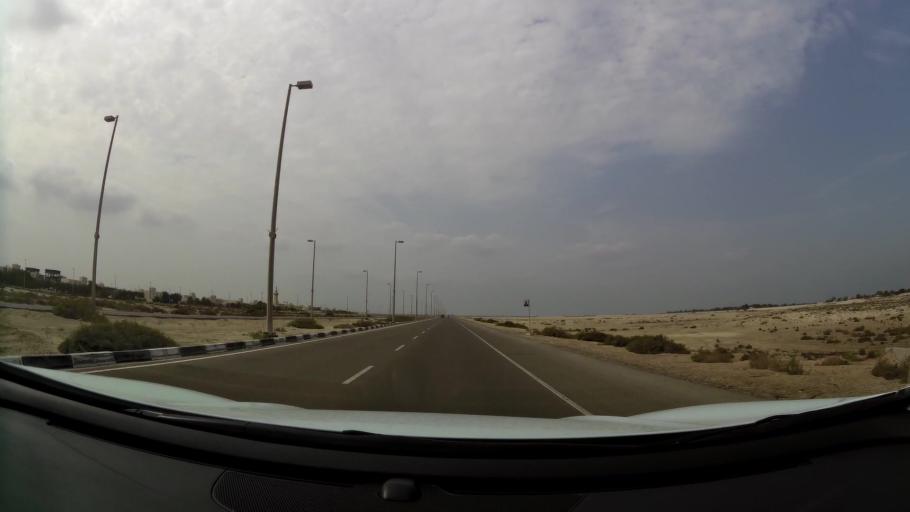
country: AE
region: Abu Dhabi
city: Abu Dhabi
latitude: 24.6484
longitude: 54.6733
